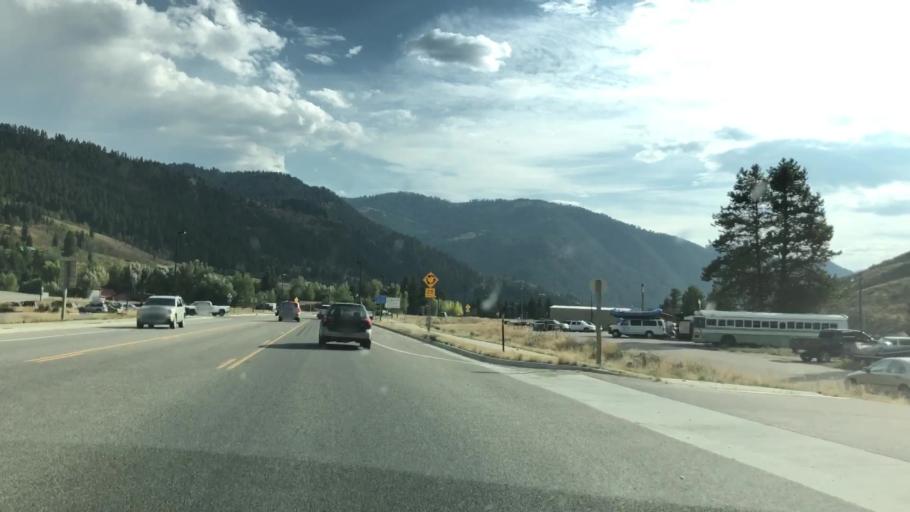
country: US
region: Wyoming
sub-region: Teton County
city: Hoback
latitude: 43.3242
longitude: -110.7300
